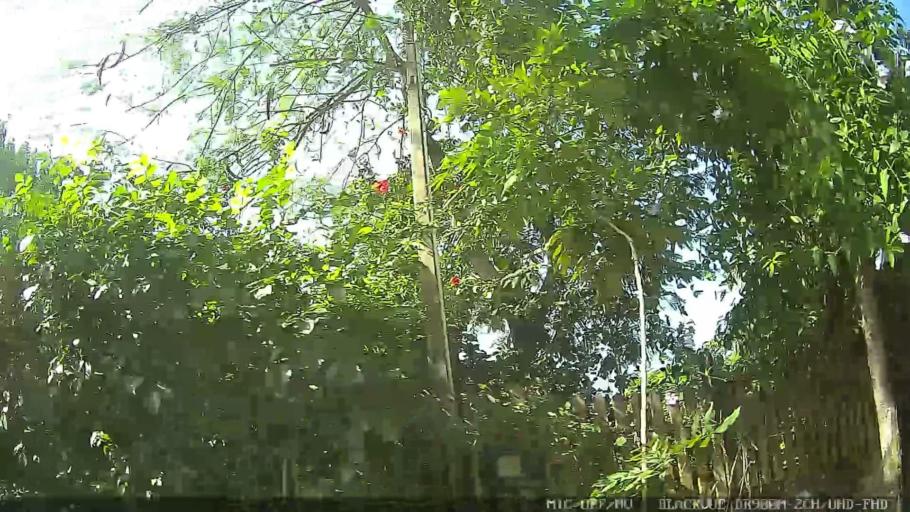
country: BR
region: Sao Paulo
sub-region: Guaruja
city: Guaruja
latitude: -23.9868
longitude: -46.1880
